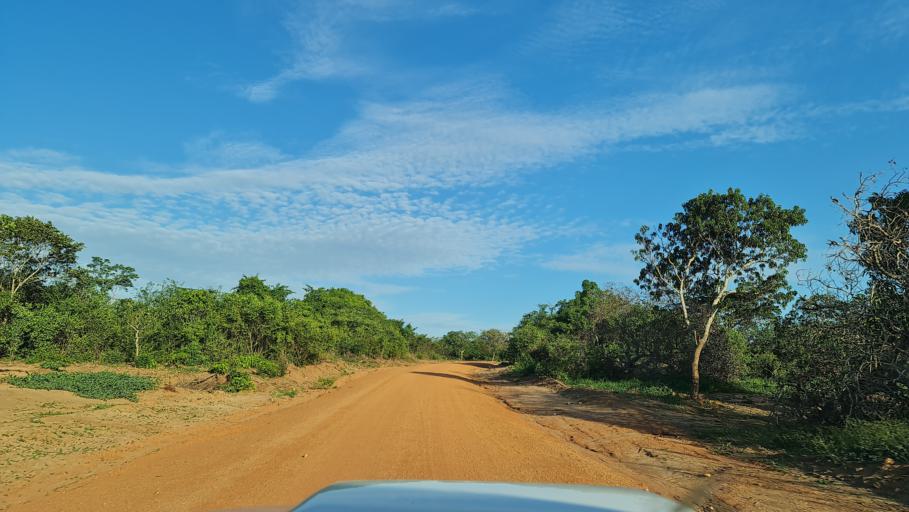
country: MZ
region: Nampula
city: Nacala
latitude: -14.6731
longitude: 40.2837
